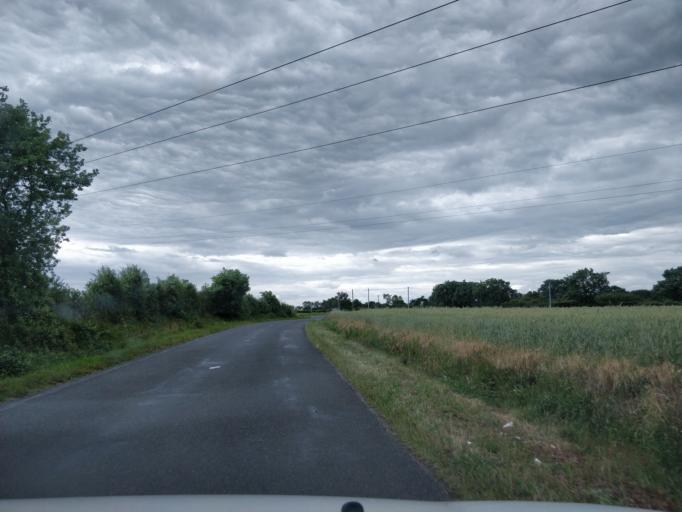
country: FR
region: Pays de la Loire
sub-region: Departement de Maine-et-Loire
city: Feneu
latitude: 47.6233
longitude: -0.6252
